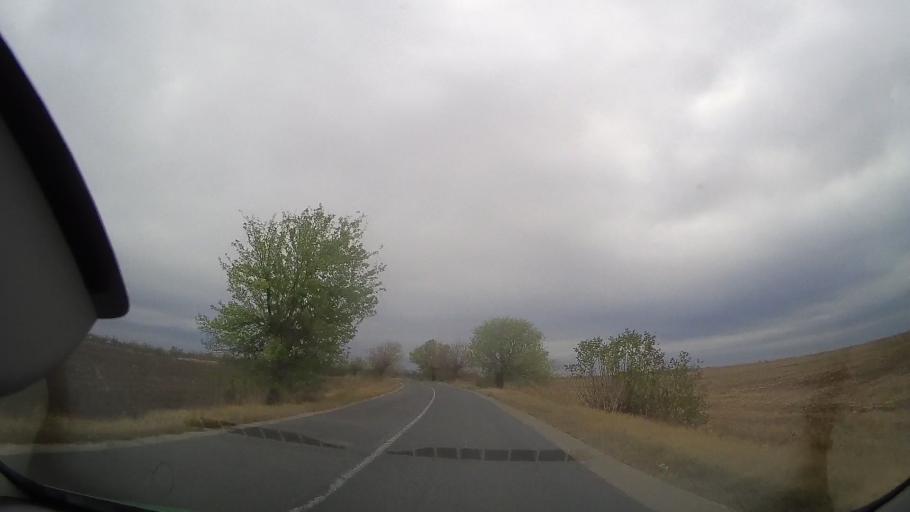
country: RO
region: Buzau
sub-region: Comuna Padina
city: Padina
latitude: 44.7790
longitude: 27.1544
